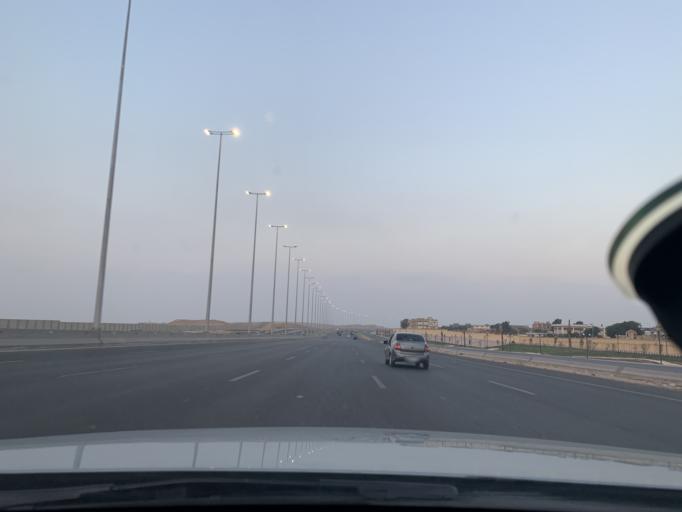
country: EG
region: Muhafazat al Qalyubiyah
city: Al Khankah
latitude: 30.0916
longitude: 31.4710
